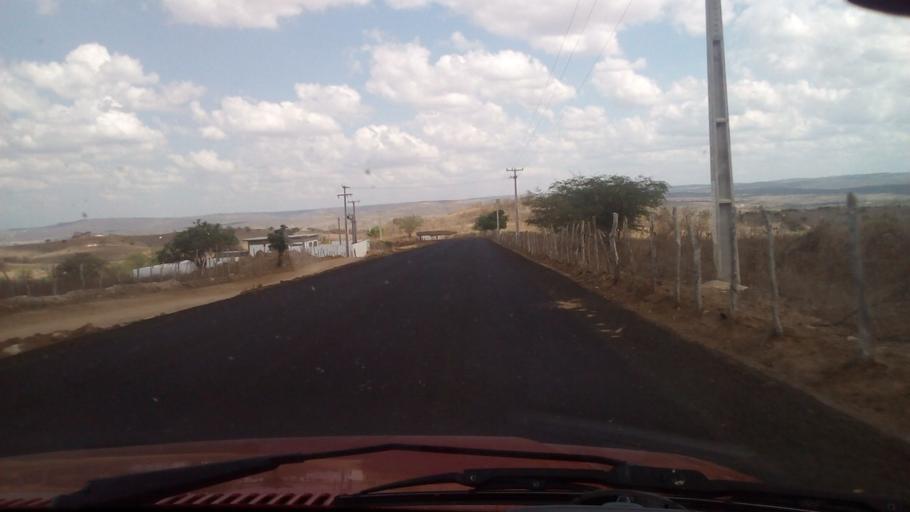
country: BR
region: Paraiba
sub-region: Cacimba De Dentro
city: Cacimba de Dentro
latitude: -6.6577
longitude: -35.7649
